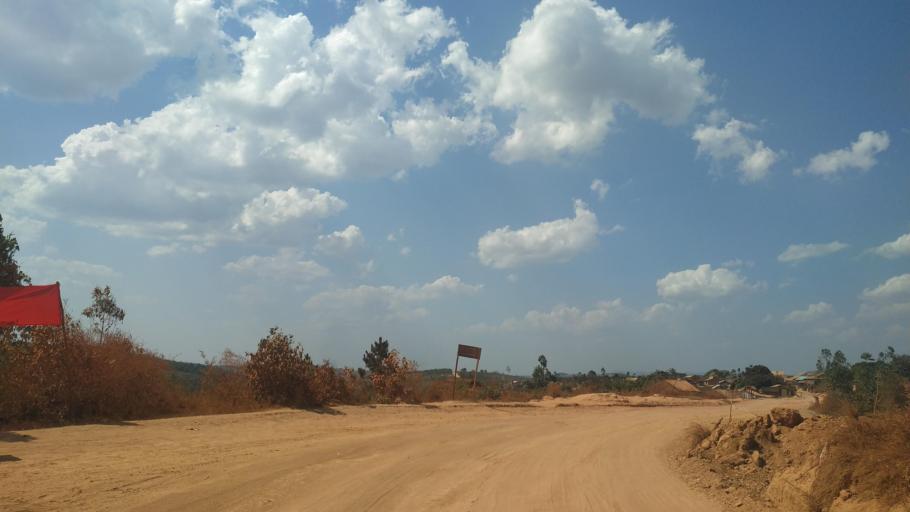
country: MG
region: Alaotra Mangoro
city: Ambatondrazaka
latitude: -18.0791
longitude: 48.2566
